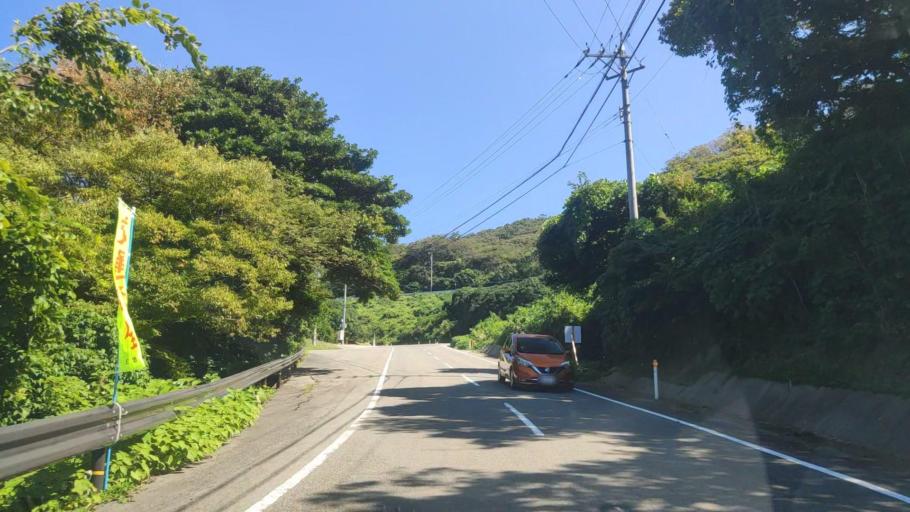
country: JP
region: Ishikawa
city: Nanao
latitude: 37.5272
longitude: 137.2668
